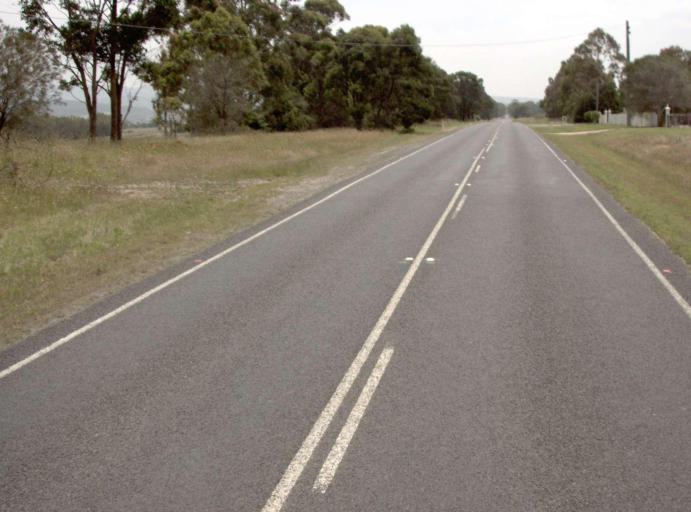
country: AU
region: Victoria
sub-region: Latrobe
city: Traralgon
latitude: -38.4993
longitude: 146.7114
